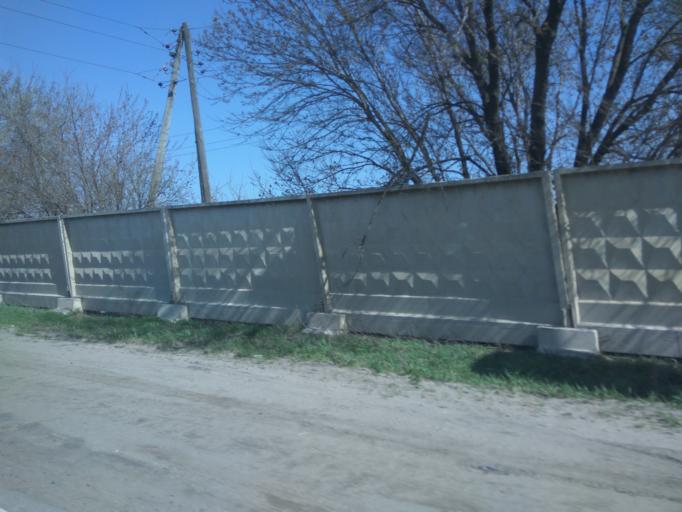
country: RU
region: Moskovskaya
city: Ramenskoye
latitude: 55.5502
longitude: 38.2620
